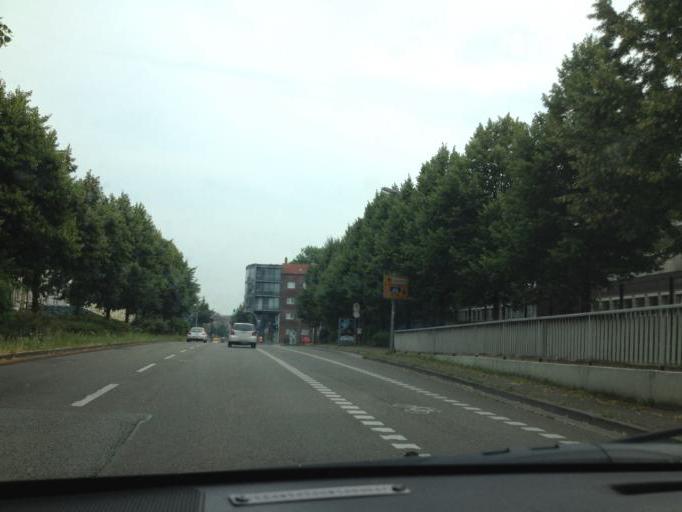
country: DE
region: North Rhine-Westphalia
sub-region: Regierungsbezirk Arnsberg
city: Dortmund
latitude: 51.4996
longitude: 7.4594
